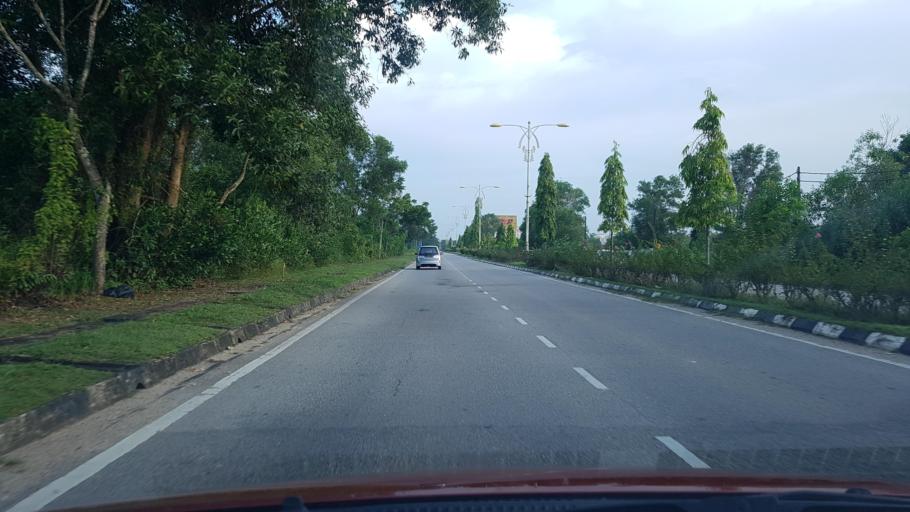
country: MY
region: Terengganu
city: Kuala Terengganu
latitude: 5.3551
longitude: 103.1036
